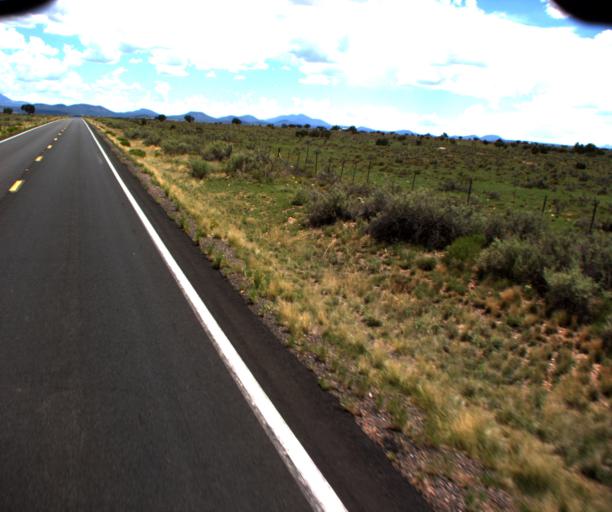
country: US
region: Arizona
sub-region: Coconino County
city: Williams
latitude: 35.6316
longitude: -112.1185
